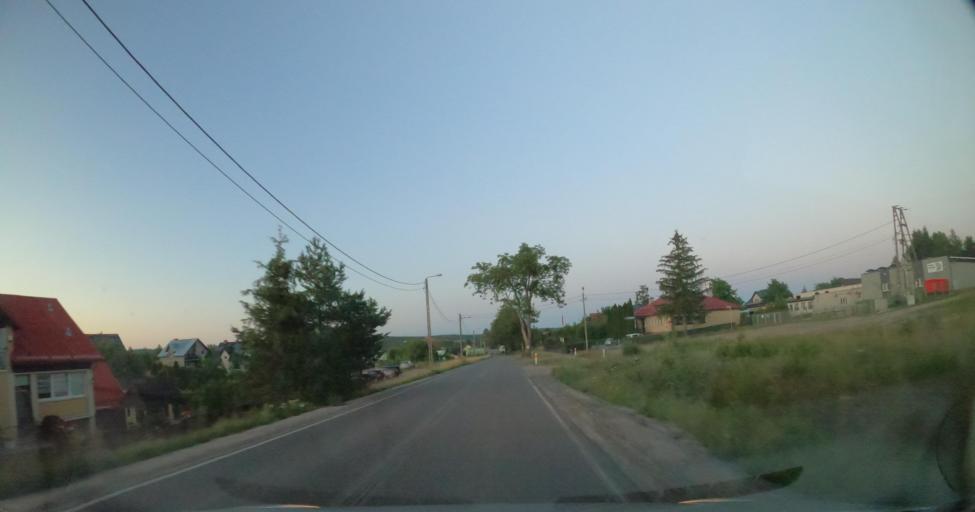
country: PL
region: Pomeranian Voivodeship
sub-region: Powiat wejherowski
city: Szemud
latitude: 54.4844
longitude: 18.2153
